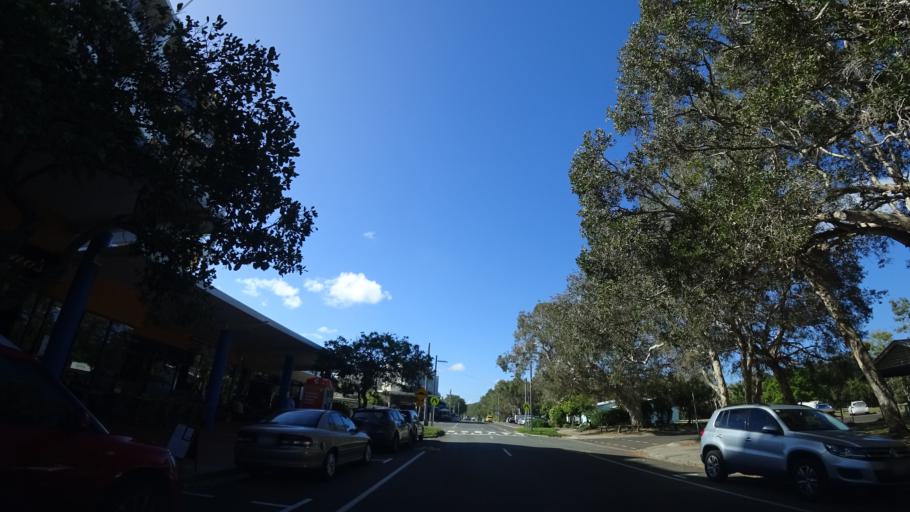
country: AU
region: Queensland
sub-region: Sunshine Coast
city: Mooloolaba
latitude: -26.6155
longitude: 153.1006
